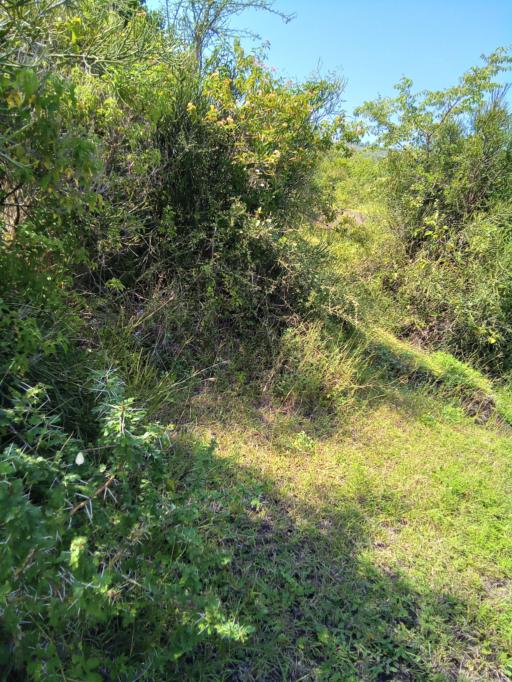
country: KE
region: Homa Bay
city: Homa Bay
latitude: -0.4712
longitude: 34.1866
